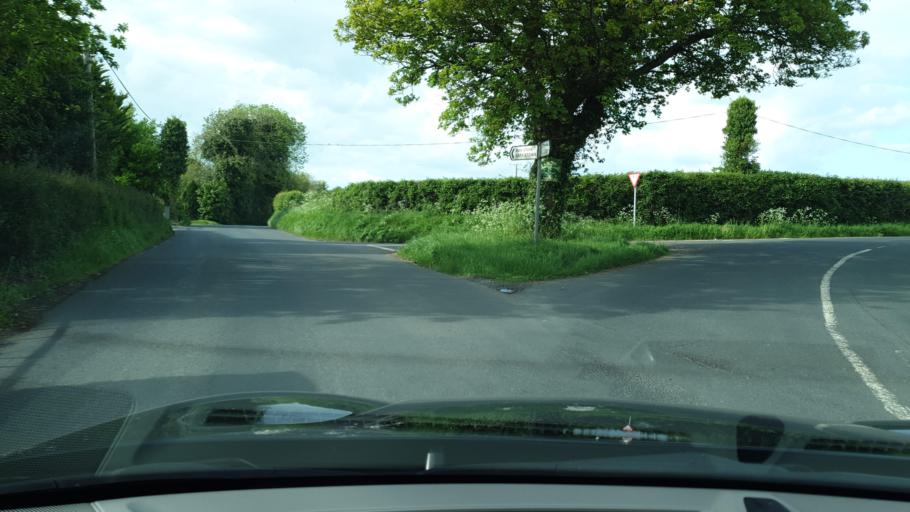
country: IE
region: Leinster
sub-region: An Mhi
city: Ashbourne
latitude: 53.5340
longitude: -6.4061
